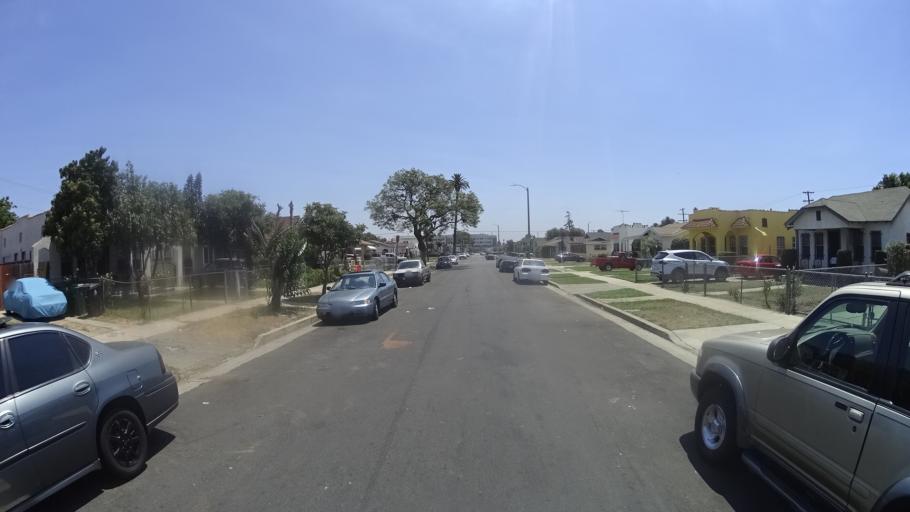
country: US
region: California
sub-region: Los Angeles County
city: Westmont
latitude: 33.9627
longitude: -118.2968
